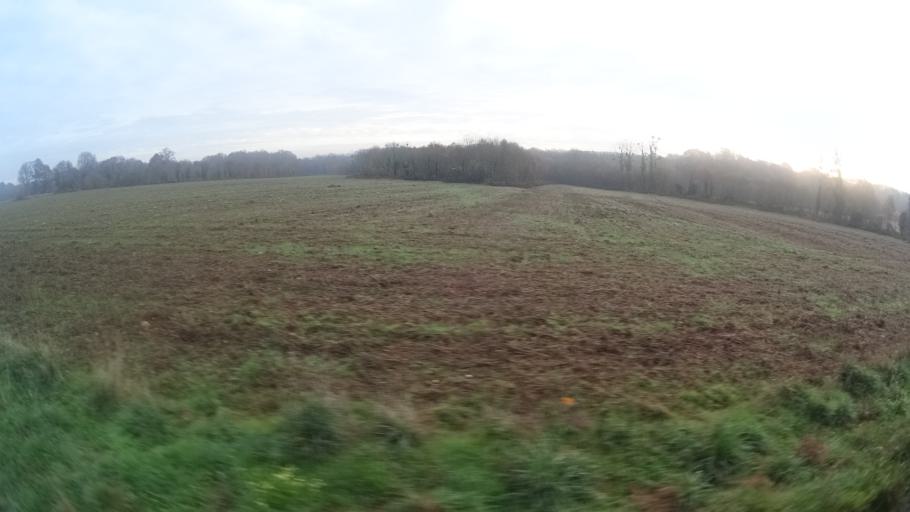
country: FR
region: Pays de la Loire
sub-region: Departement de la Loire-Atlantique
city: Avessac
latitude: 47.6468
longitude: -2.0242
